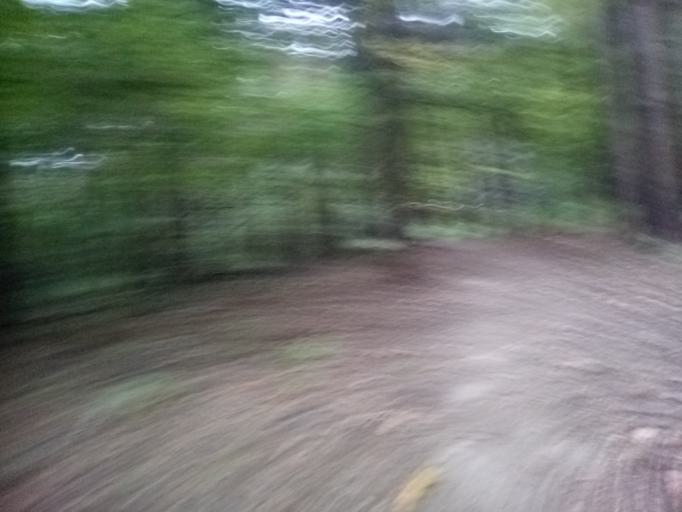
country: RU
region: Moscow
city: Novo-Peredelkino
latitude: 55.6195
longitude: 37.3258
